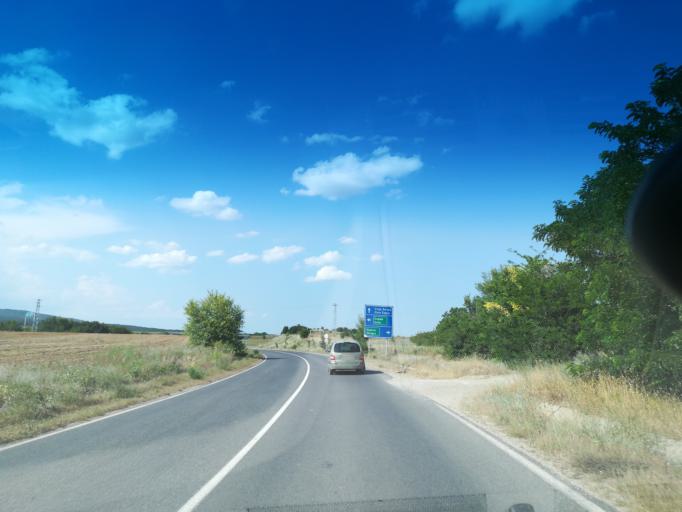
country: BG
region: Stara Zagora
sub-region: Obshtina Chirpan
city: Chirpan
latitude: 42.2472
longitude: 25.4118
